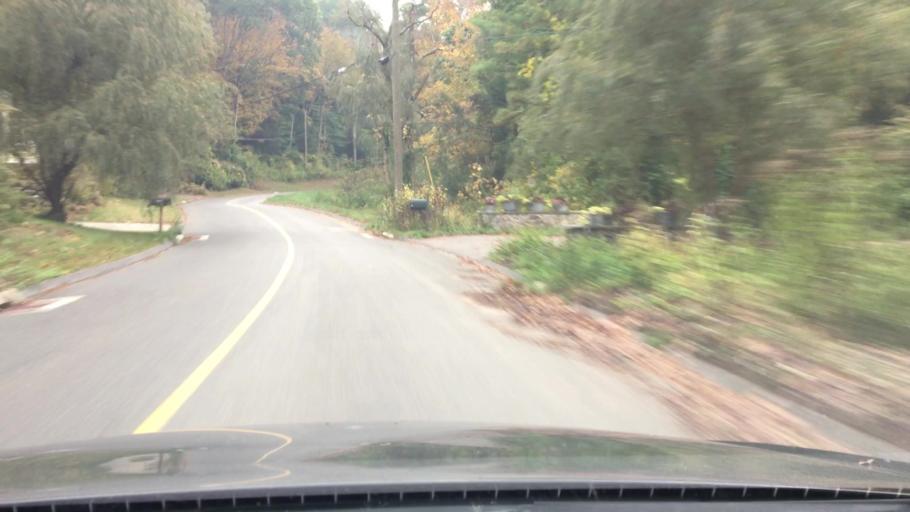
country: US
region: Connecticut
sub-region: New Haven County
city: Heritage Village
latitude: 41.5087
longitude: -73.2709
